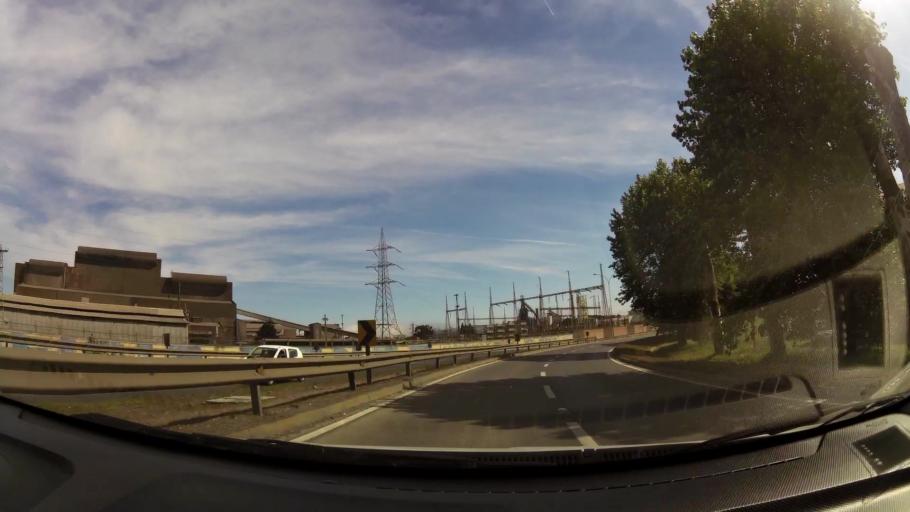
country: CL
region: Biobio
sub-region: Provincia de Concepcion
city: Talcahuano
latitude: -36.7494
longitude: -73.1245
